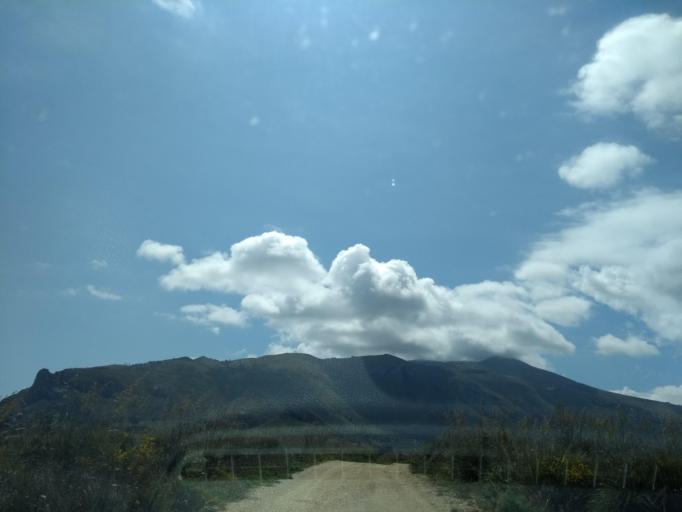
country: IT
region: Sicily
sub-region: Trapani
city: Castellammare del Golfo
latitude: 38.0477
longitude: 12.8478
